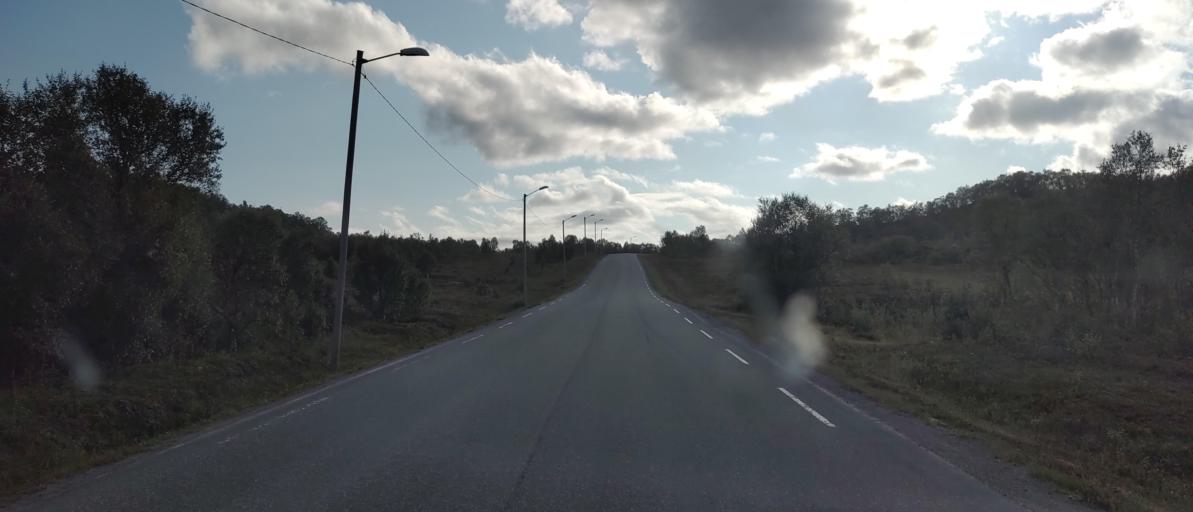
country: NO
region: Nordland
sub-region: Sortland
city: Sortland
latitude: 68.7221
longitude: 15.4676
